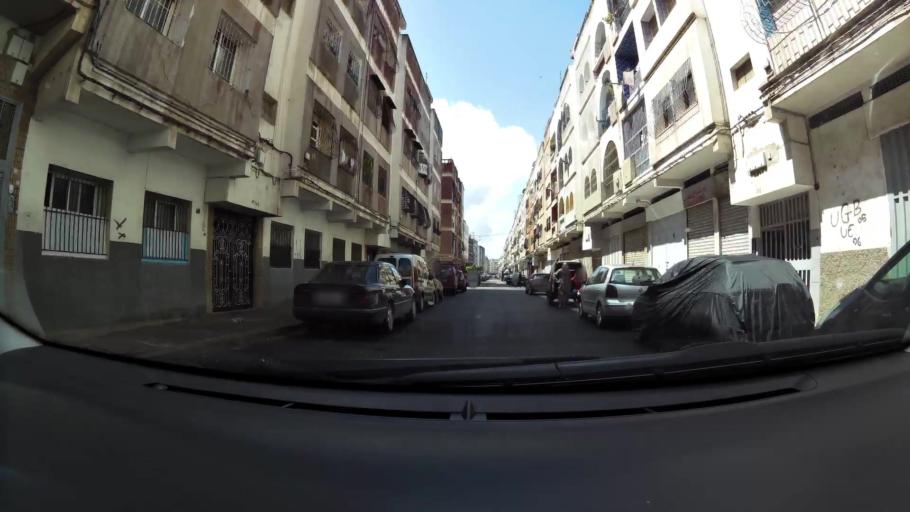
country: MA
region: Grand Casablanca
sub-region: Mediouna
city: Tit Mellil
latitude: 33.5419
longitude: -7.5522
